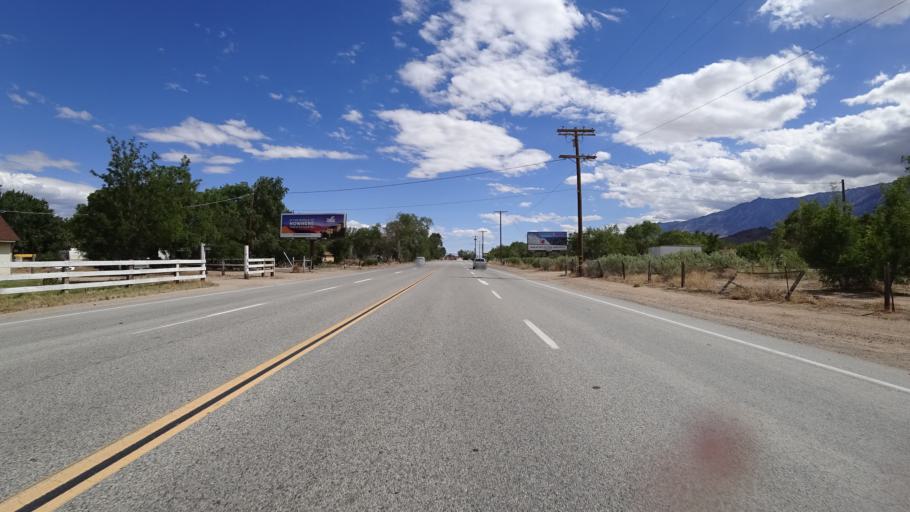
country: US
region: California
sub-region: Inyo County
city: Lone Pine
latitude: 36.5967
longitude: -118.0590
